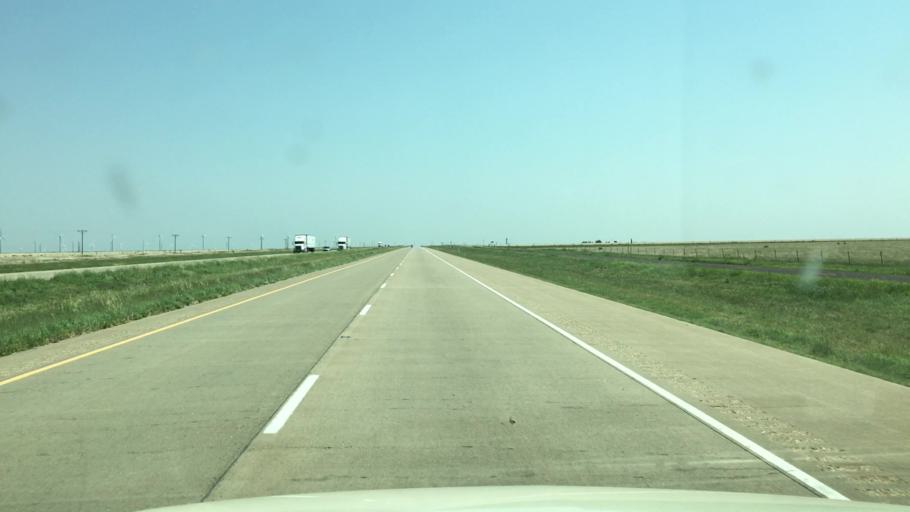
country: US
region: Texas
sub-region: Oldham County
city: Vega
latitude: 35.2726
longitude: -102.6156
